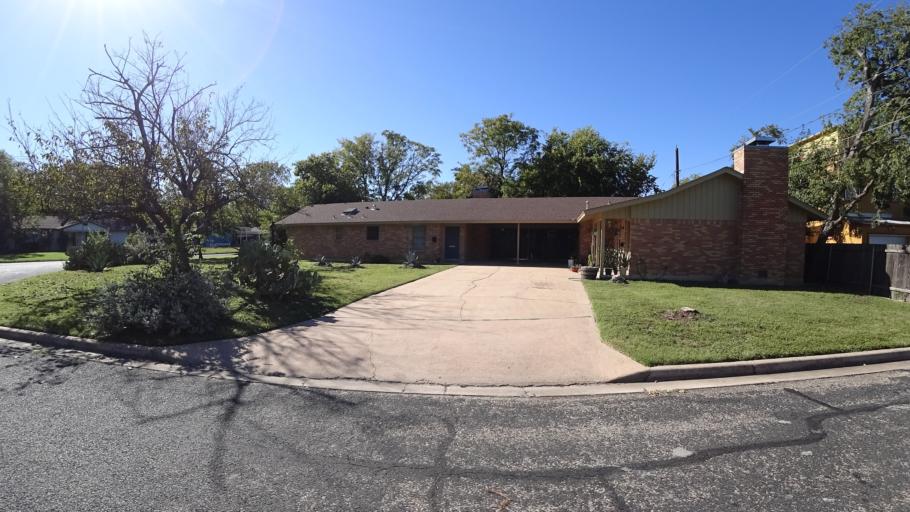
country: US
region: Texas
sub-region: Travis County
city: Rollingwood
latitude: 30.2355
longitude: -97.7861
